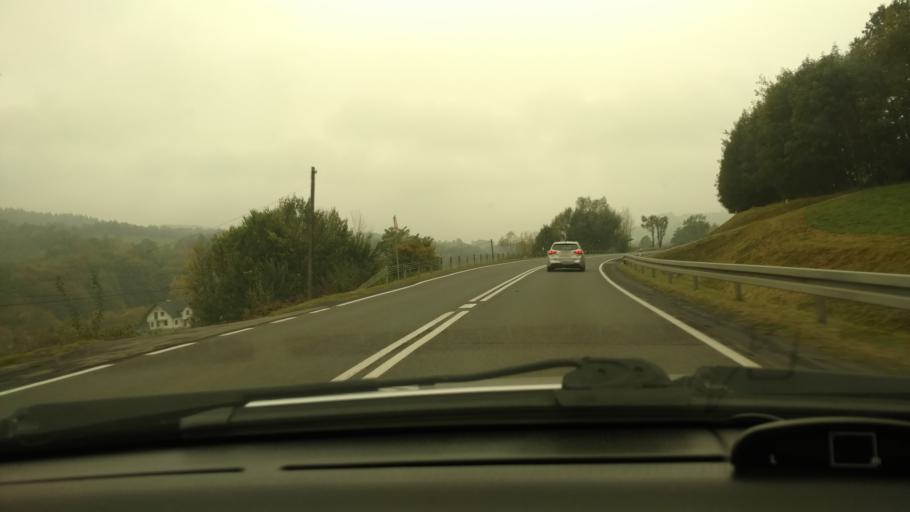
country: PL
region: Lesser Poland Voivodeship
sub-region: Powiat nowosadecki
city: Grybow
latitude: 49.6230
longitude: 20.9317
